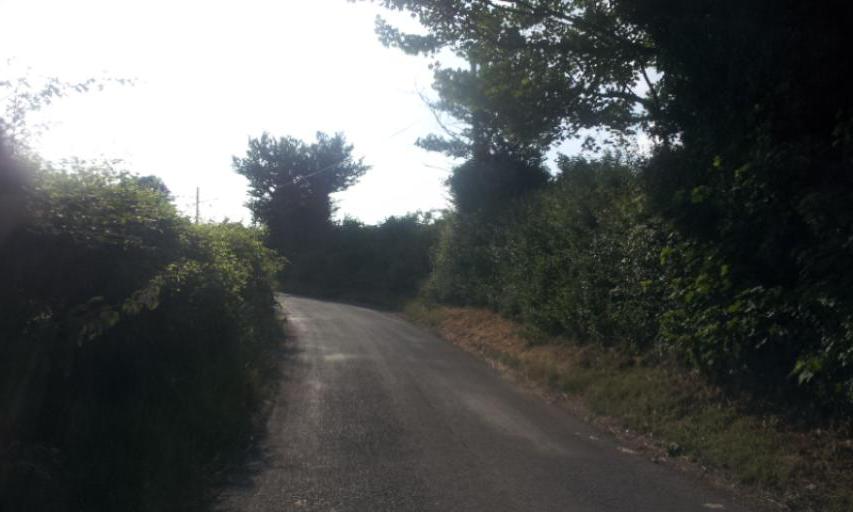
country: GB
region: England
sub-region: Kent
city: Boxley
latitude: 51.2875
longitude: 0.6007
